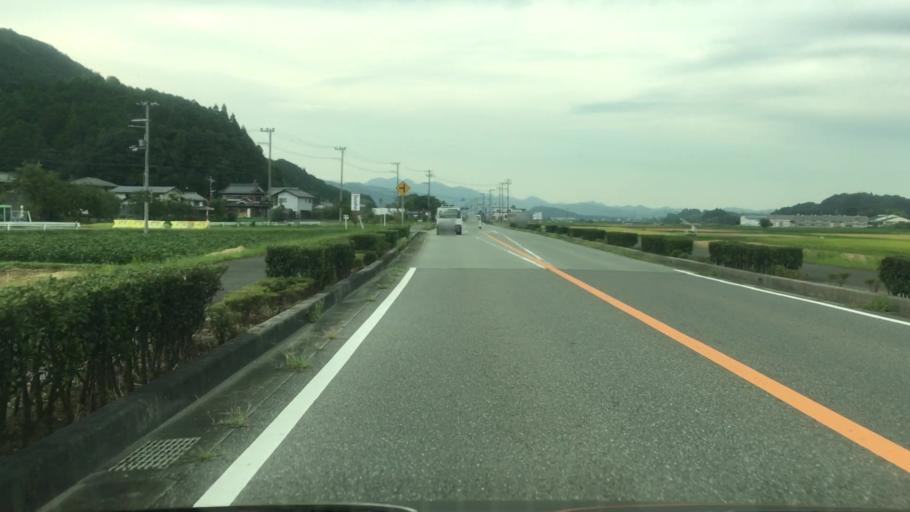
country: JP
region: Hyogo
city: Sasayama
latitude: 35.0703
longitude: 135.2677
